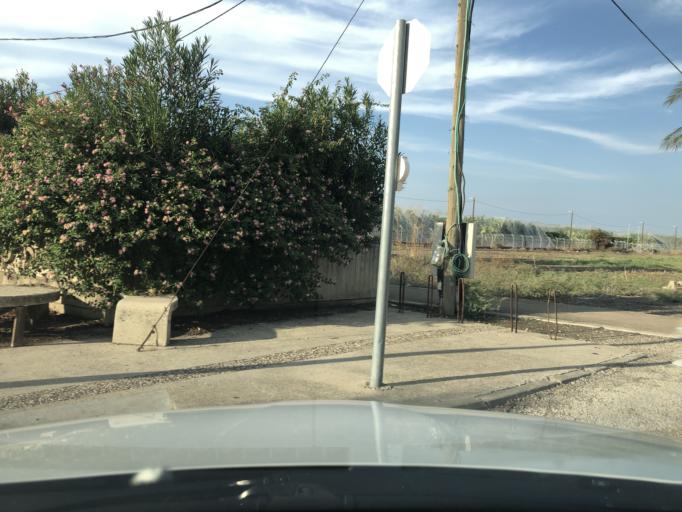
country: IL
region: Northern District
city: Yavne'el
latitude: 32.6584
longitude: 35.5774
